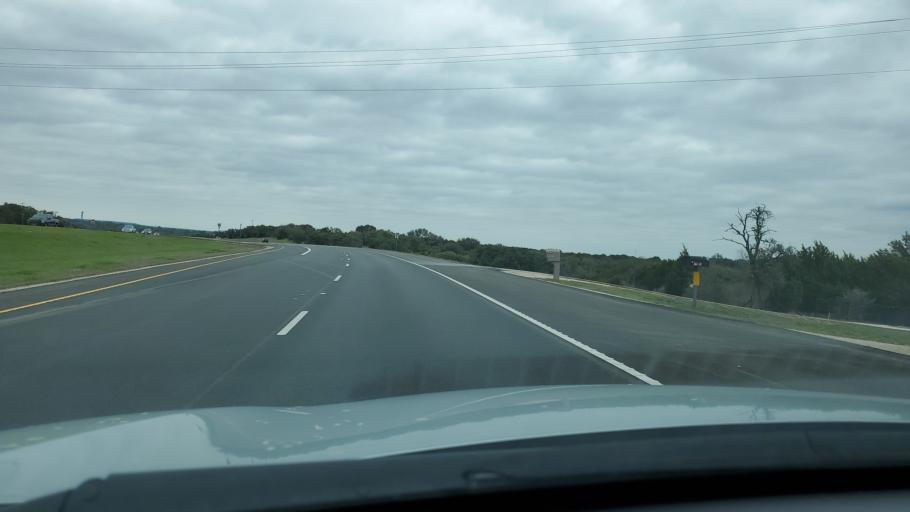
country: US
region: Texas
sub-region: Williamson County
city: Florence
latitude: 30.9446
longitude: -97.7846
